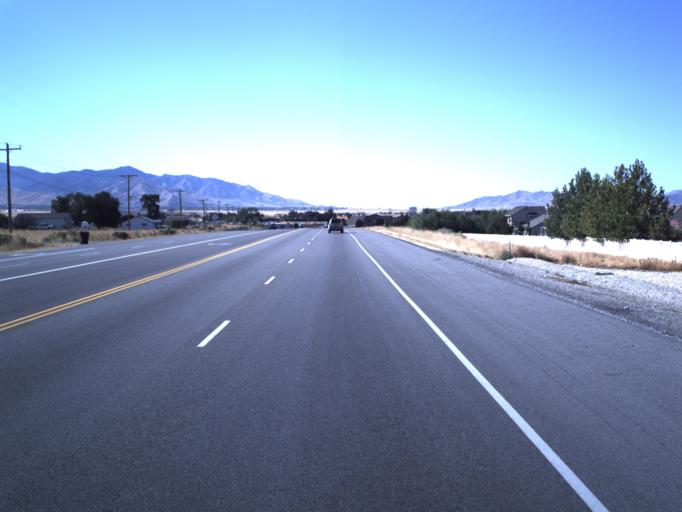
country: US
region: Utah
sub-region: Tooele County
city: Stansbury park
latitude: 40.6297
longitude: -112.2914
